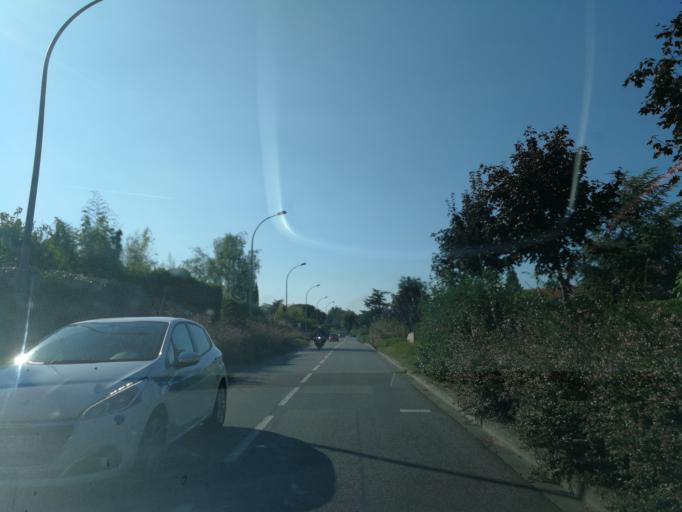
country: FR
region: Midi-Pyrenees
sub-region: Departement de la Haute-Garonne
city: Balma
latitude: 43.6197
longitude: 1.5158
